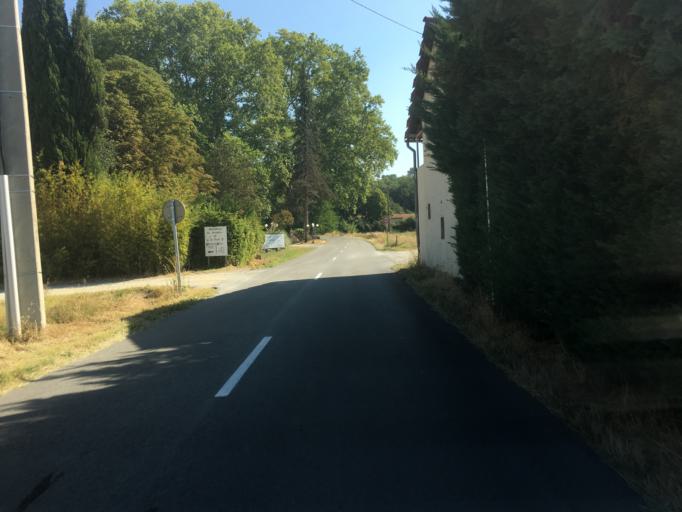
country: FR
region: Provence-Alpes-Cote d'Azur
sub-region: Departement des Alpes-de-Haute-Provence
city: Manosque
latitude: 43.8037
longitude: 5.8404
